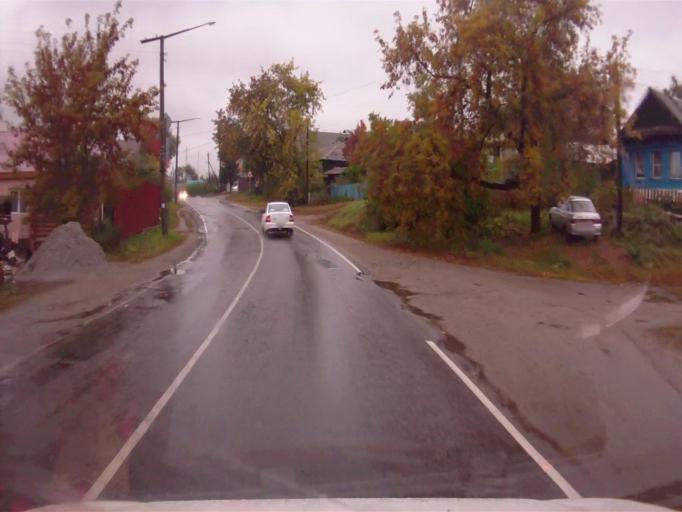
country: RU
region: Chelyabinsk
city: Kyshtym
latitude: 55.7236
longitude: 60.5263
